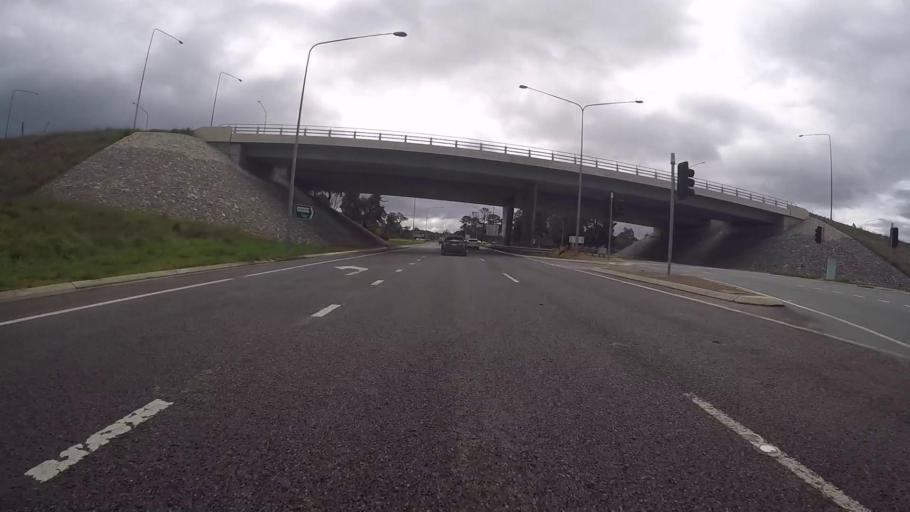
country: AU
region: Australian Capital Territory
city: Kaleen
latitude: -35.2260
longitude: 149.1225
